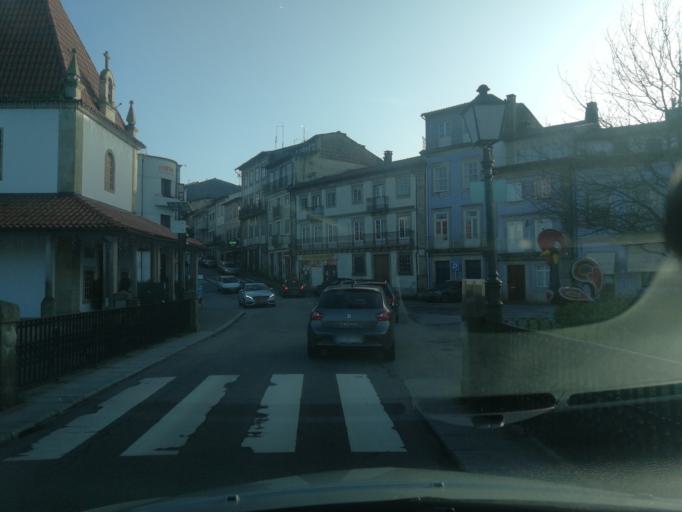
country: PT
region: Braga
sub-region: Barcelos
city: Barcelos
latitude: 41.5271
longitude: -8.6224
